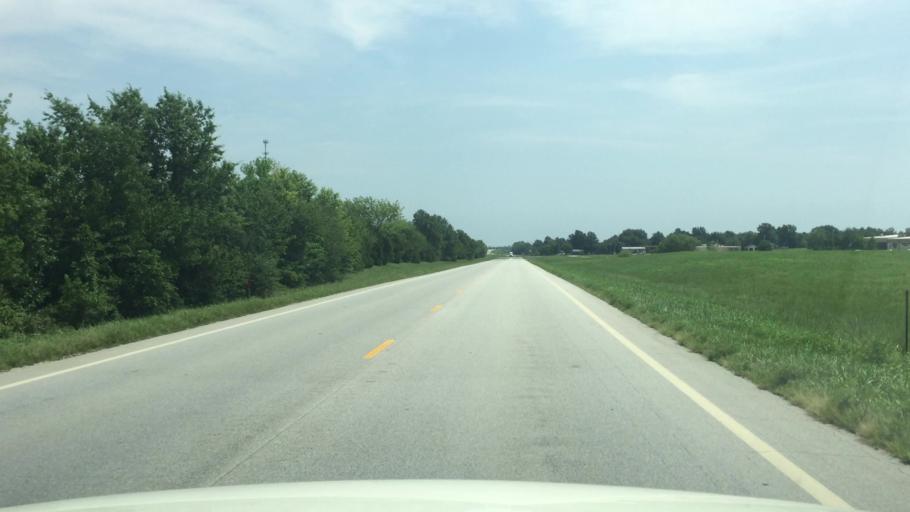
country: US
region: Kansas
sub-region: Cherokee County
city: Columbus
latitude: 37.1786
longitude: -94.8581
